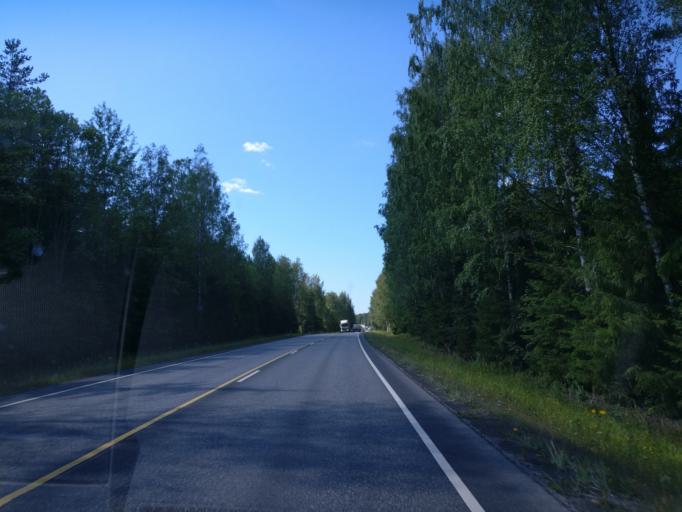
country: FI
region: Satakunta
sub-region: Pori
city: Kullaa
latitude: 61.4611
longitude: 22.1328
